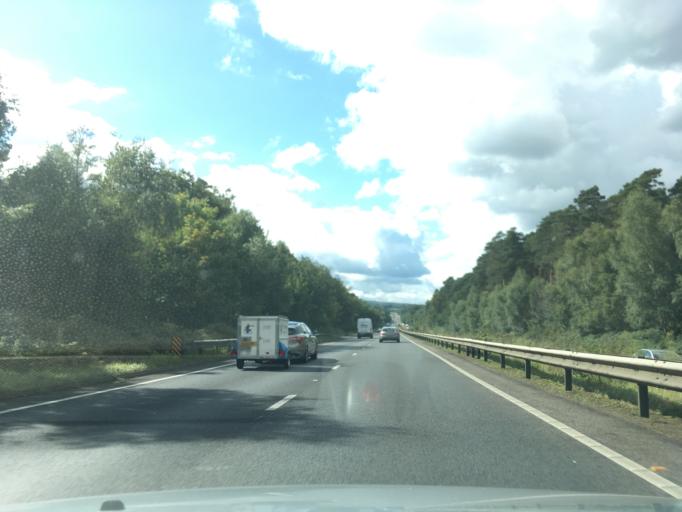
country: GB
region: England
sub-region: Surrey
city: Milford
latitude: 51.1599
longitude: -0.6753
